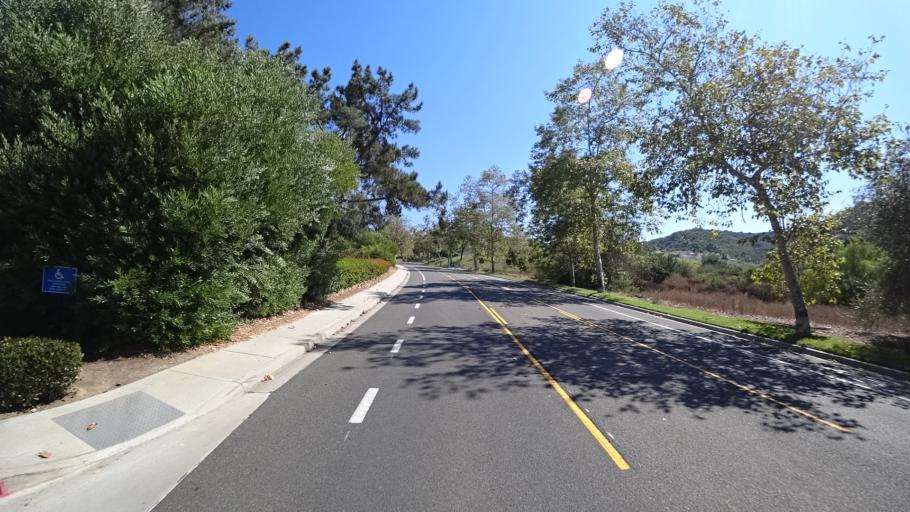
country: US
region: California
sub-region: Orange County
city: San Clemente
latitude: 33.4377
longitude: -117.5973
